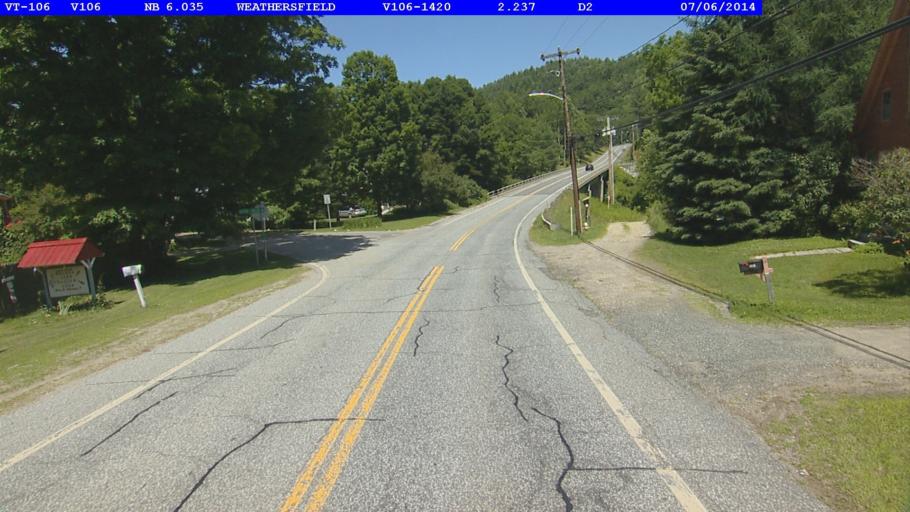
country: US
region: Vermont
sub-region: Windsor County
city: Springfield
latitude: 43.3737
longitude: -72.5139
